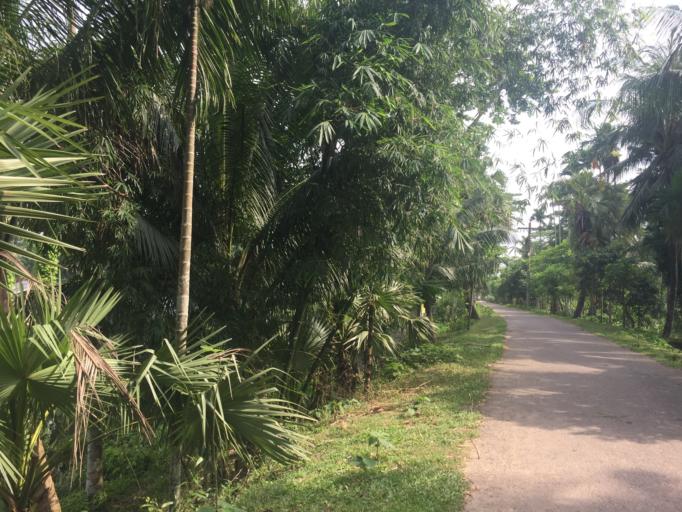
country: BD
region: Barisal
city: Mathba
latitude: 22.2284
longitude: 89.9158
